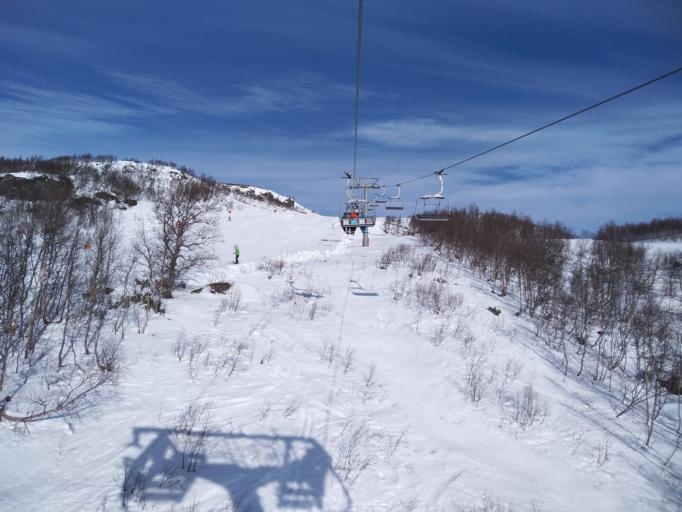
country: NO
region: Aust-Agder
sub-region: Bykle
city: Hovden
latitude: 59.5745
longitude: 7.3122
